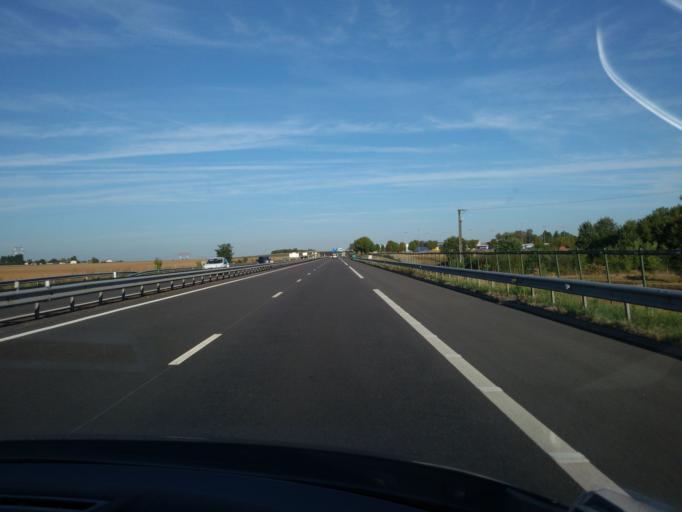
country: FR
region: Centre
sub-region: Departement du Cher
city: Trouy
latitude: 47.0399
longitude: 2.3520
